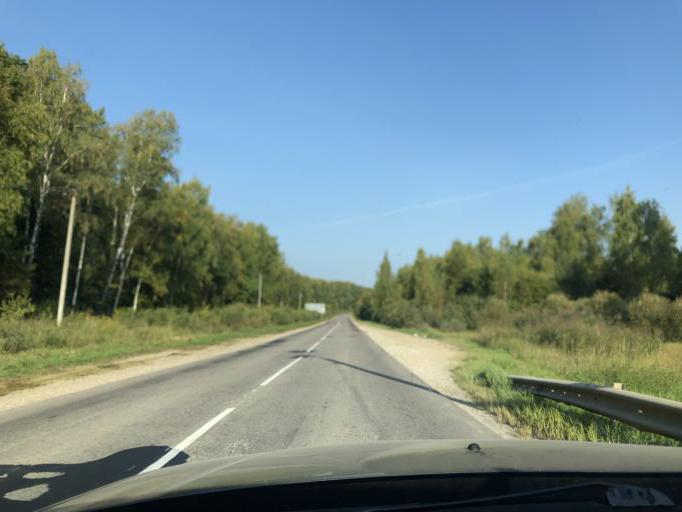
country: RU
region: Tula
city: Leninskiy
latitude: 54.3215
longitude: 37.4017
